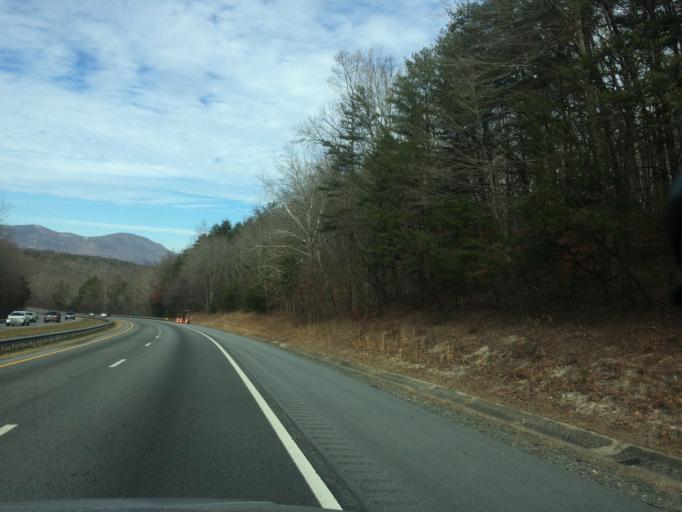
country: US
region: South Carolina
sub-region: Spartanburg County
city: Landrum
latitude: 35.2099
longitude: -82.1819
